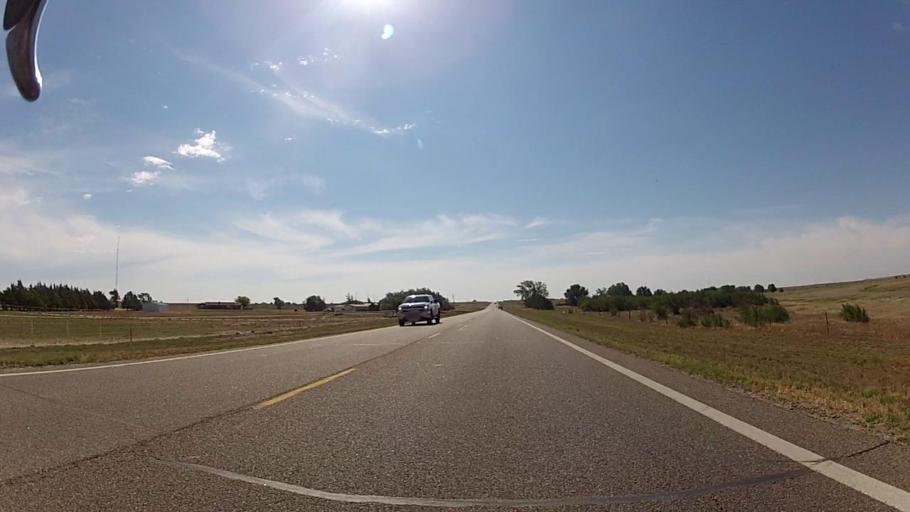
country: US
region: Kansas
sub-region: Grant County
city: Ulysses
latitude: 37.5705
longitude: -101.3304
